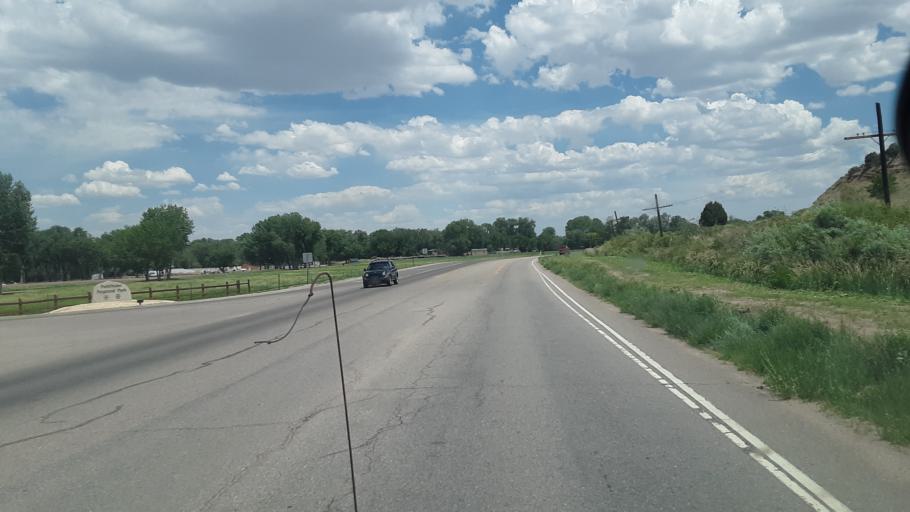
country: US
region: Colorado
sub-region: Fremont County
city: Florence
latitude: 38.4055
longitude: -105.1459
